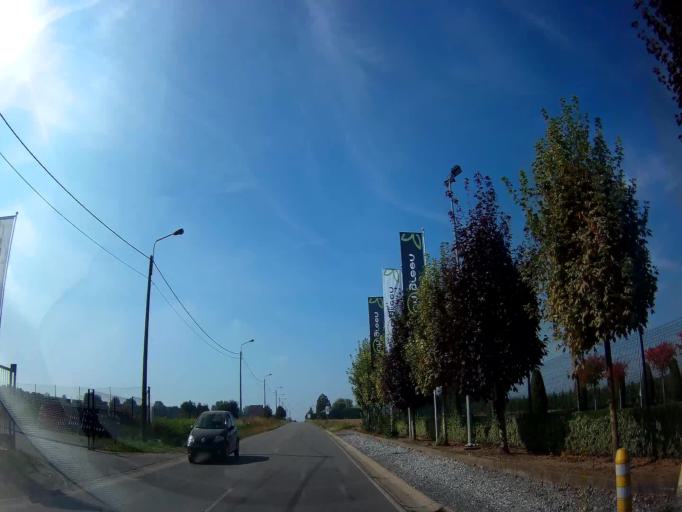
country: BE
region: Wallonia
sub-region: Province de Liege
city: Verlaine
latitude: 50.6012
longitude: 5.3460
